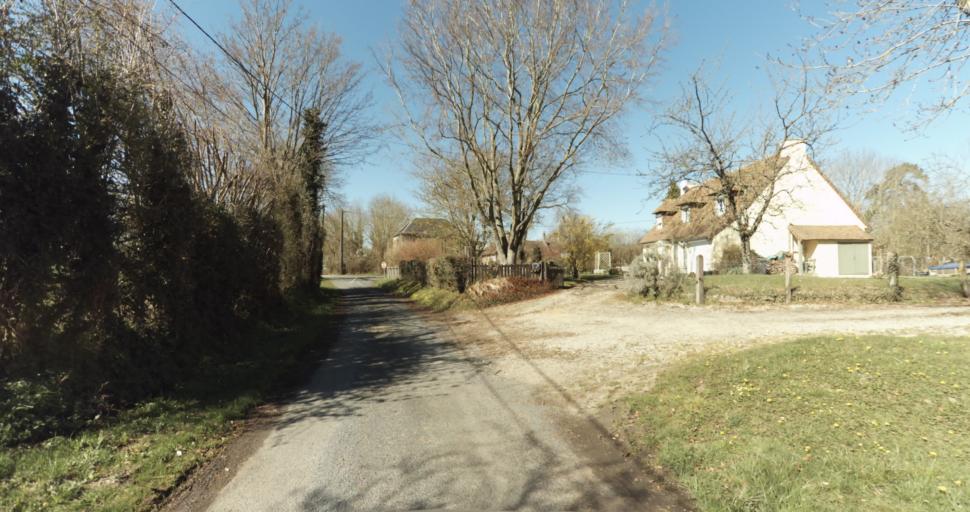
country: FR
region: Lower Normandy
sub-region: Departement du Calvados
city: Saint-Pierre-sur-Dives
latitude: 48.9615
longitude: 0.0517
